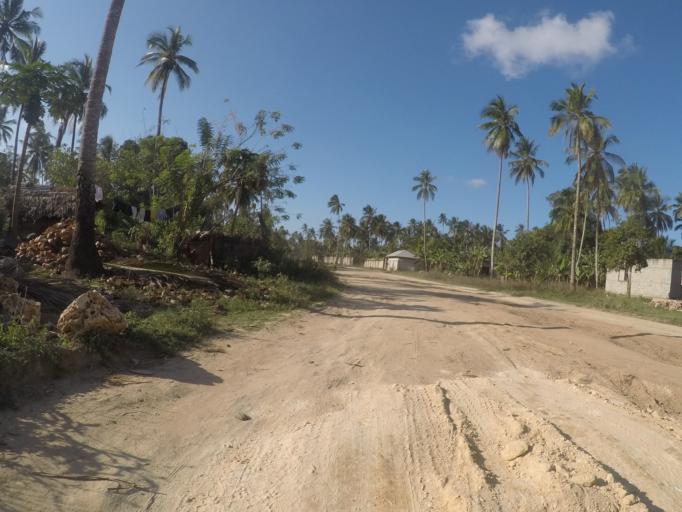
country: TZ
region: Zanzibar Central/South
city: Koani
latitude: -6.1668
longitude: 39.2865
